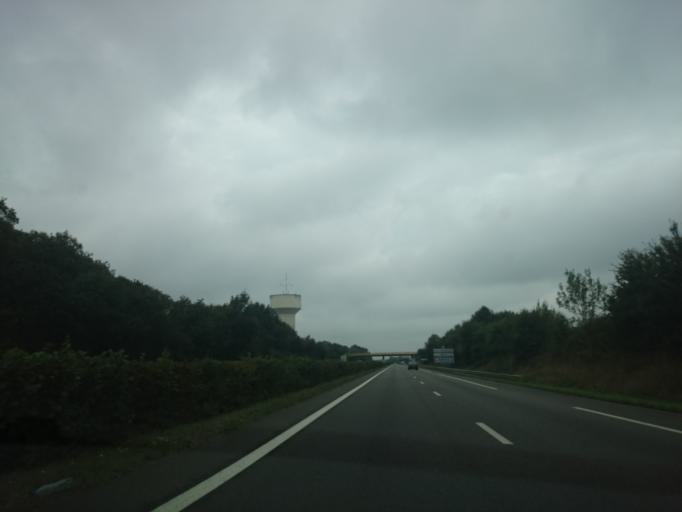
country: FR
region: Pays de la Loire
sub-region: Departement de la Loire-Atlantique
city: Bouguenais
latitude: 47.1649
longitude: -1.6369
